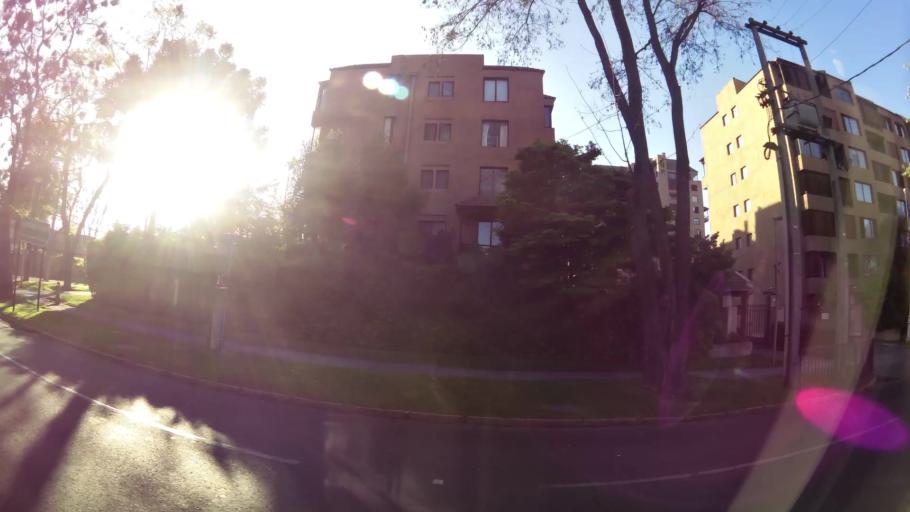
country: CL
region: Santiago Metropolitan
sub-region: Provincia de Santiago
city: Villa Presidente Frei, Nunoa, Santiago, Chile
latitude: -33.3994
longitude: -70.5657
